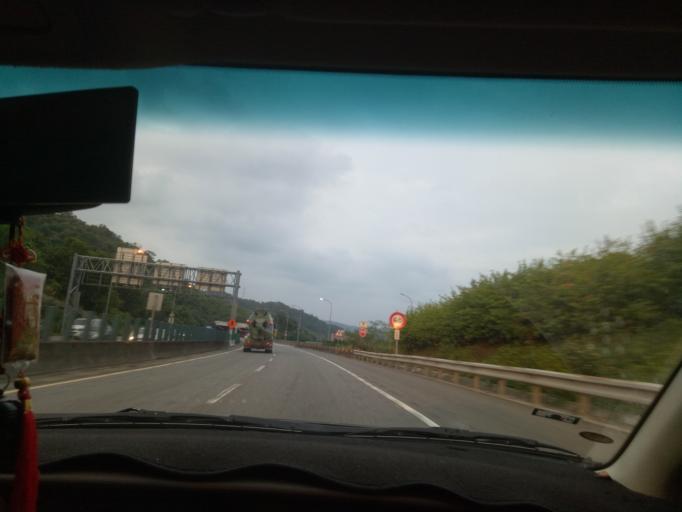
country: TW
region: Taiwan
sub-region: Keelung
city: Keelung
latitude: 25.0985
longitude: 121.7054
